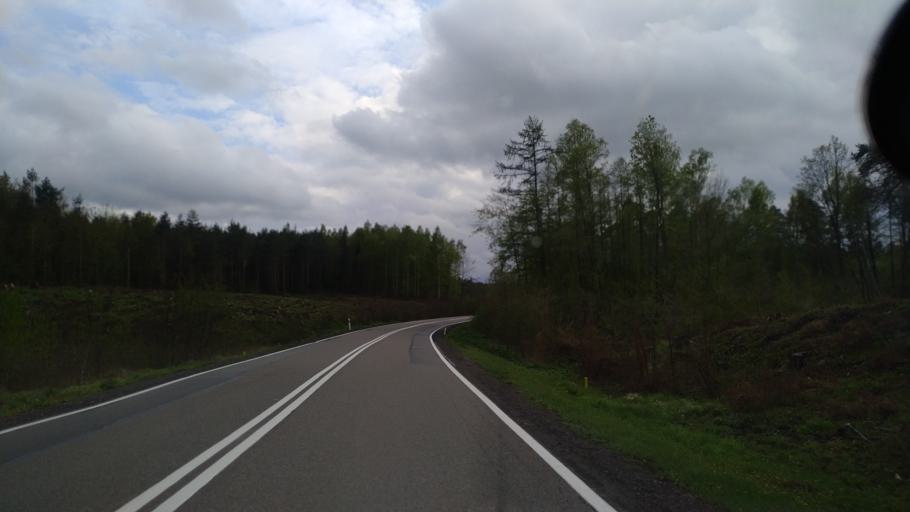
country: PL
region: Pomeranian Voivodeship
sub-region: Powiat kwidzynski
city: Ryjewo
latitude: 53.8202
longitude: 18.9813
